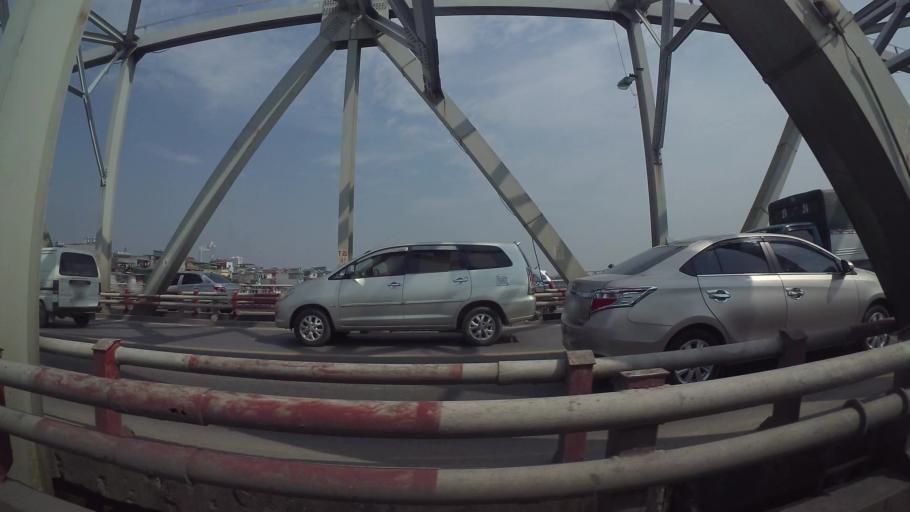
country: VN
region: Ha Noi
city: Hoan Kiem
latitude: 21.0360
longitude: 105.8580
